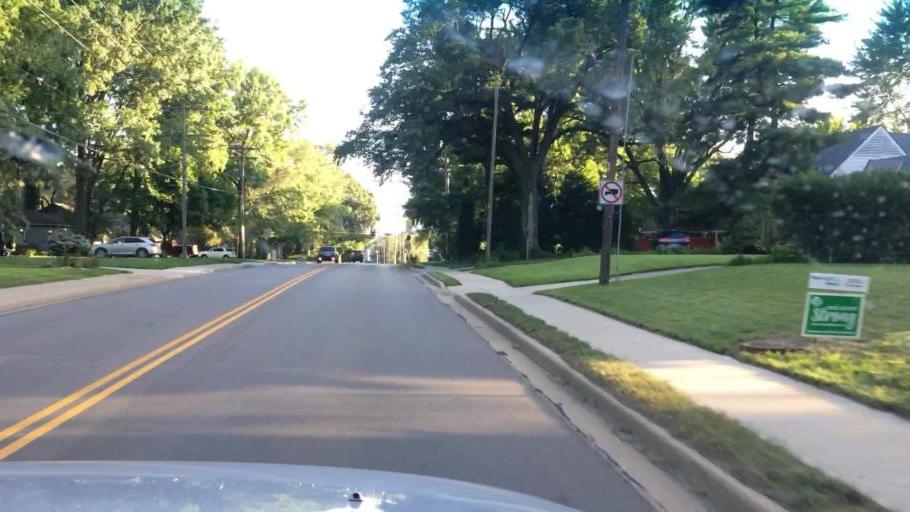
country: US
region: Kansas
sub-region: Johnson County
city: Fairway
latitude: 39.0167
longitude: -94.6304
